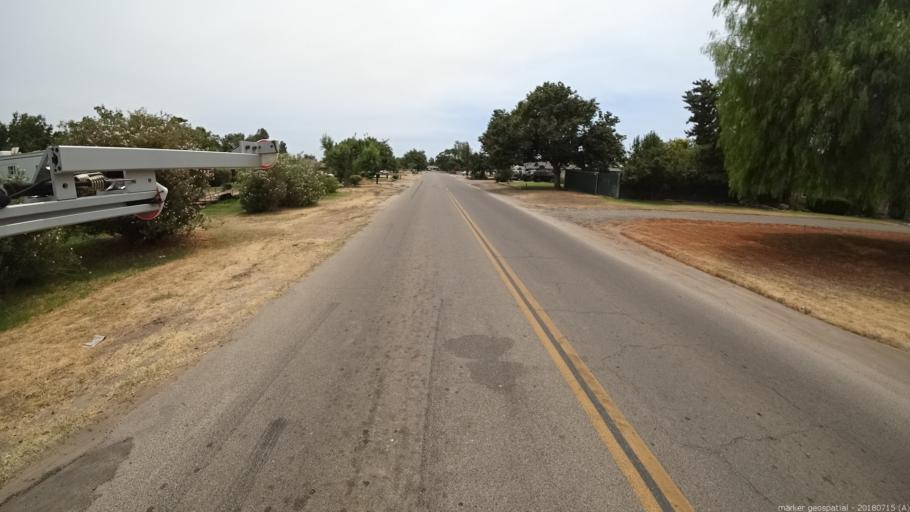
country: US
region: California
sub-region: Madera County
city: Madera Acres
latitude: 36.9990
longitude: -120.0788
